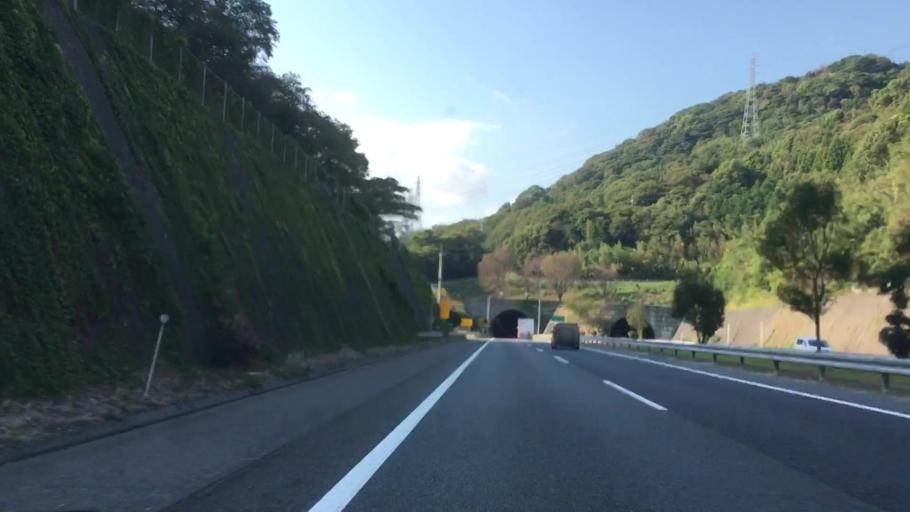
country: JP
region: Yamaguchi
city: Tokuyama
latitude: 34.0595
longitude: 131.8366
